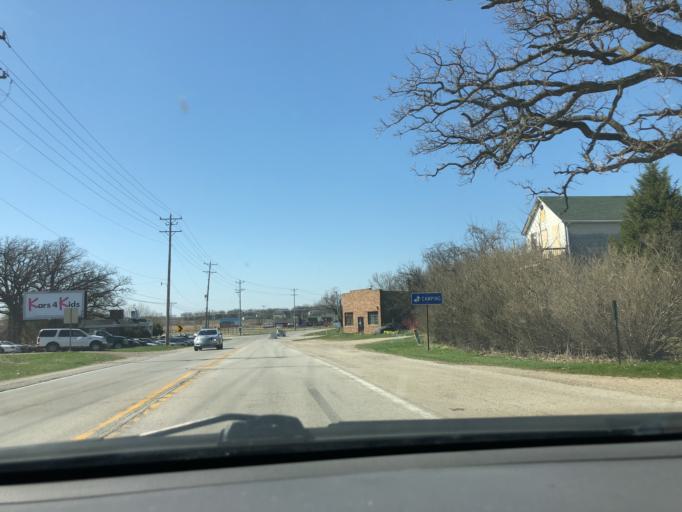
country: US
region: Illinois
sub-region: Kane County
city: Hampshire
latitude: 42.1599
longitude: -88.5255
